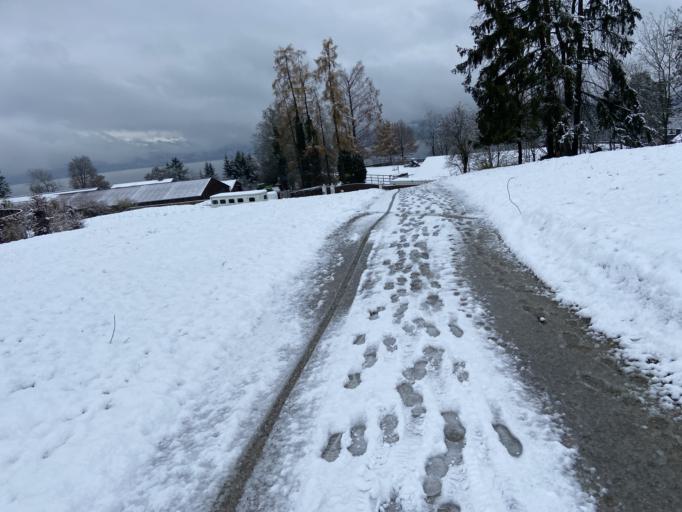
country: CH
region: Zurich
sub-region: Bezirk Meilen
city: Maennedorf / Ausserfeld
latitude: 47.2550
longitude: 8.7161
